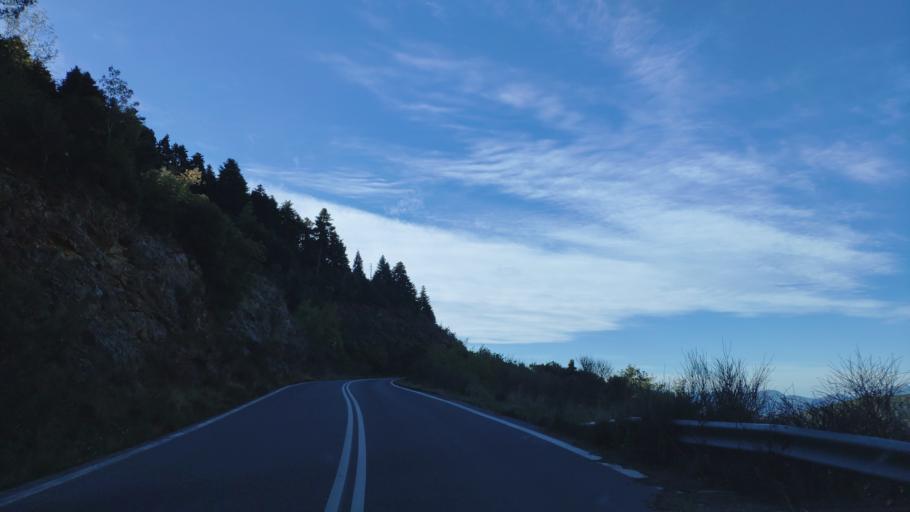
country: GR
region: Peloponnese
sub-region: Nomos Arkadias
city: Dimitsana
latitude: 37.5797
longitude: 22.0618
